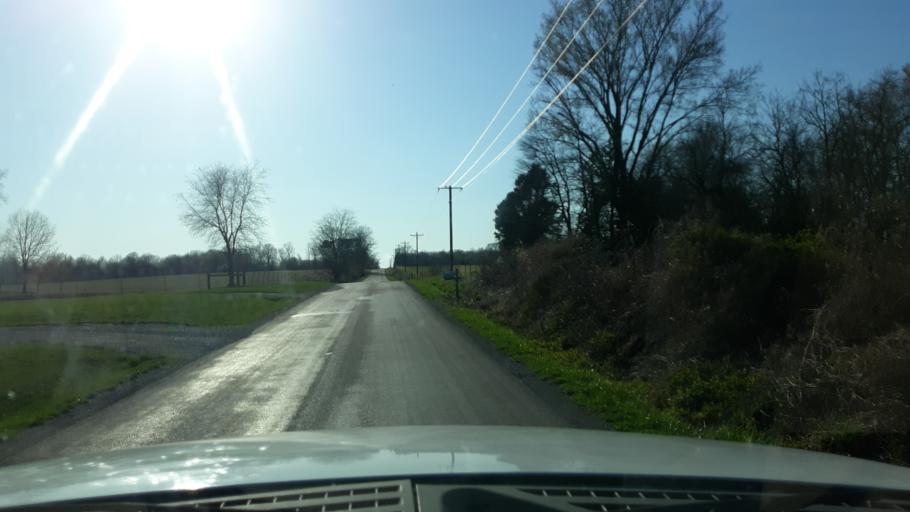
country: US
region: Illinois
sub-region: Saline County
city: Harrisburg
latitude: 37.8049
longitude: -88.6085
